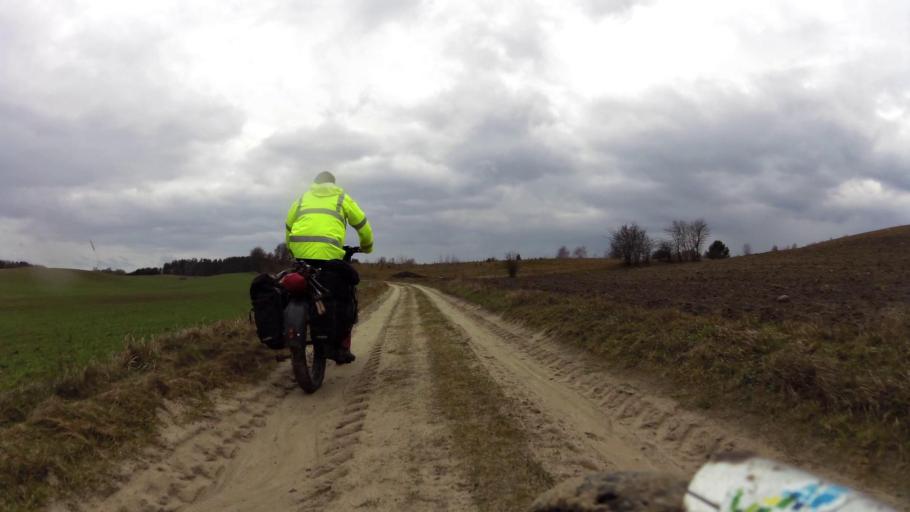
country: PL
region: Pomeranian Voivodeship
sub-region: Powiat bytowski
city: Miastko
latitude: 54.0184
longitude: 17.0080
